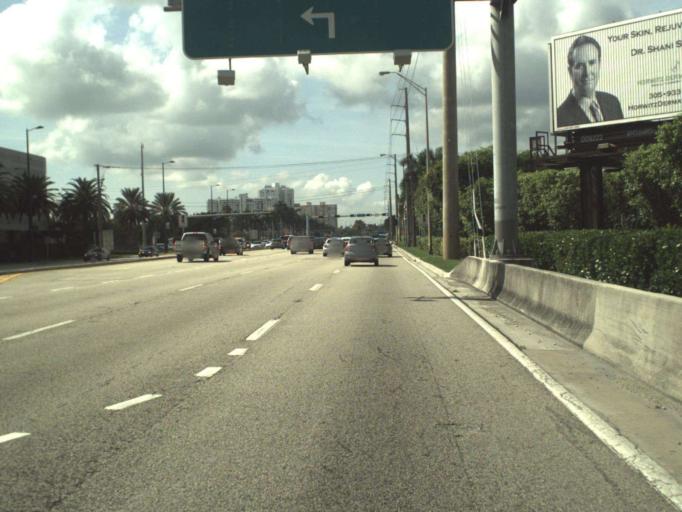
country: US
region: Florida
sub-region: Miami-Dade County
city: Aventura
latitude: 25.9569
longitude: -80.1470
